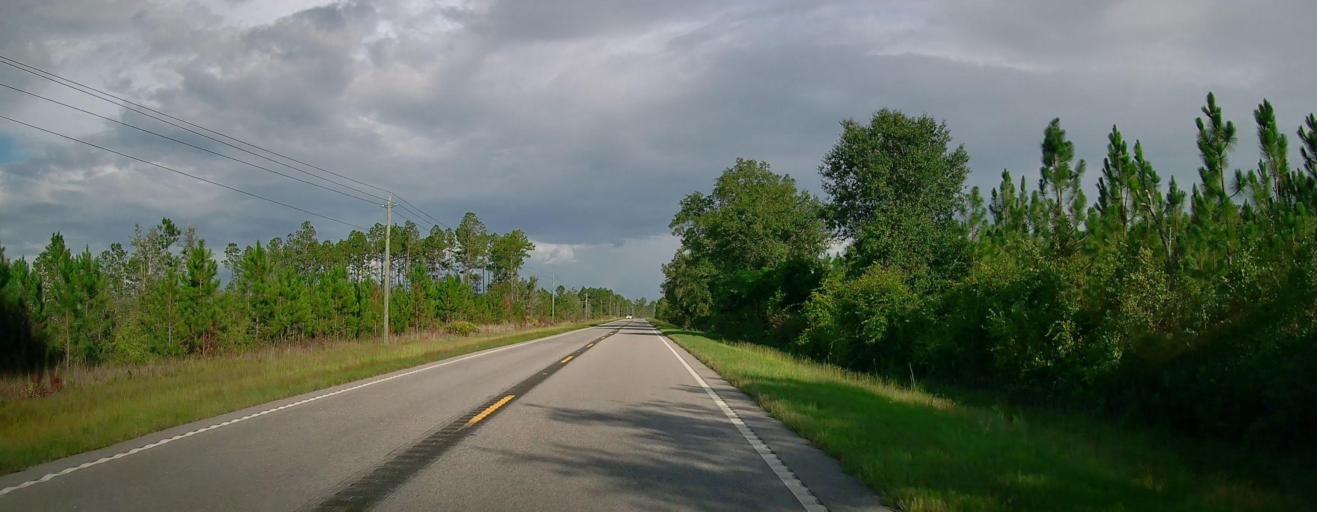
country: US
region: Georgia
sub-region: Coffee County
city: Nicholls
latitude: 31.3868
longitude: -82.6527
